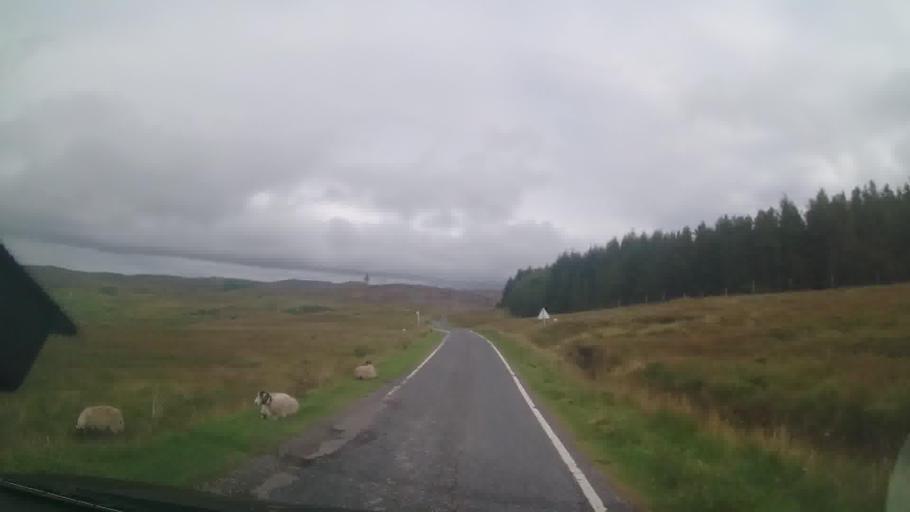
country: GB
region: Scotland
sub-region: Argyll and Bute
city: Isle Of Mull
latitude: 56.7244
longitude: -6.0459
